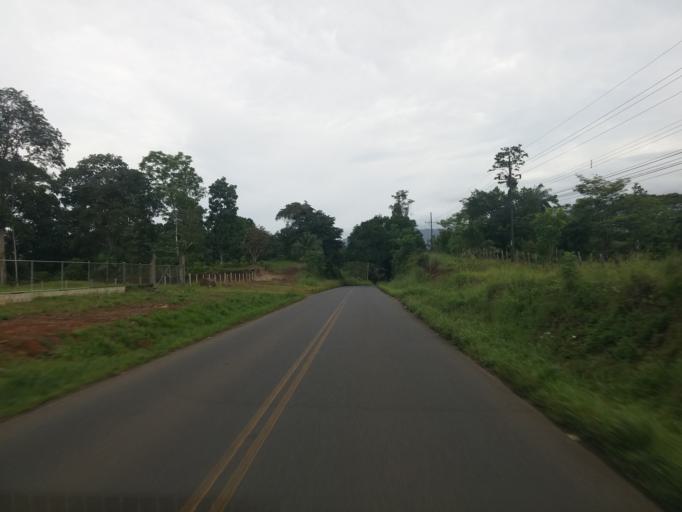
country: CR
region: Alajuela
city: Upala
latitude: 10.8484
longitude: -85.0398
